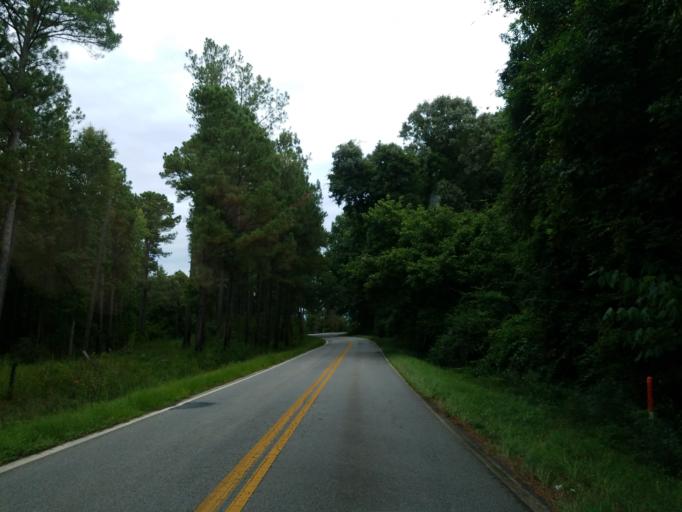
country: US
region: Georgia
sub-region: Monroe County
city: Forsyth
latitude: 32.9112
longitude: -83.8984
